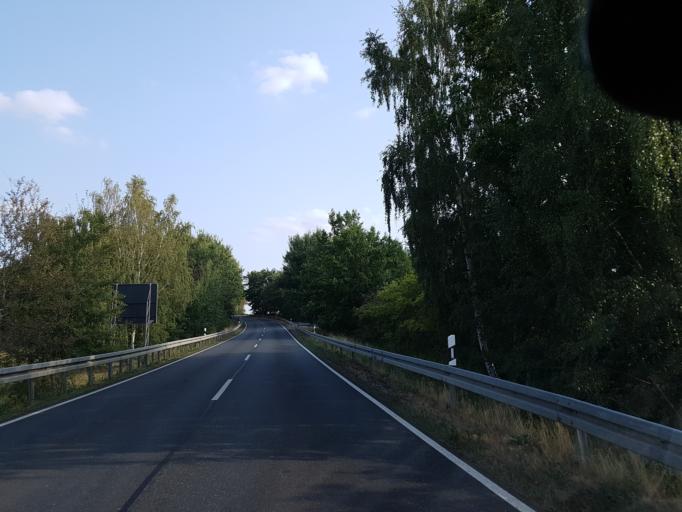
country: DE
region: Saxony-Anhalt
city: Pretzsch
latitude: 51.6743
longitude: 12.8320
